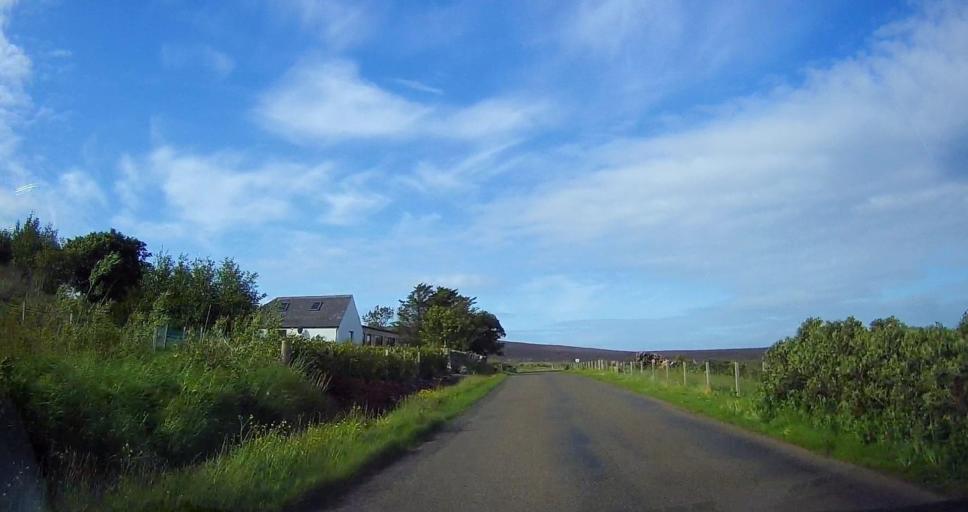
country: GB
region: Scotland
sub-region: Orkney Islands
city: Stromness
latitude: 58.7957
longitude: -3.2534
